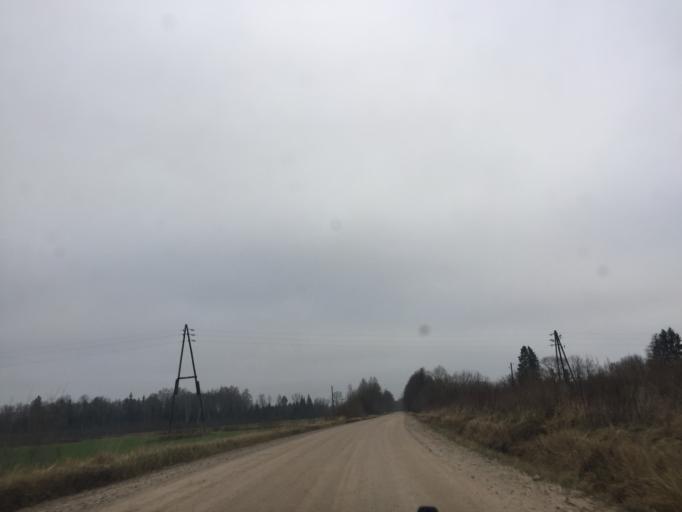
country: LV
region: Limbazu Rajons
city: Limbazi
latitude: 57.5818
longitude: 24.5136
